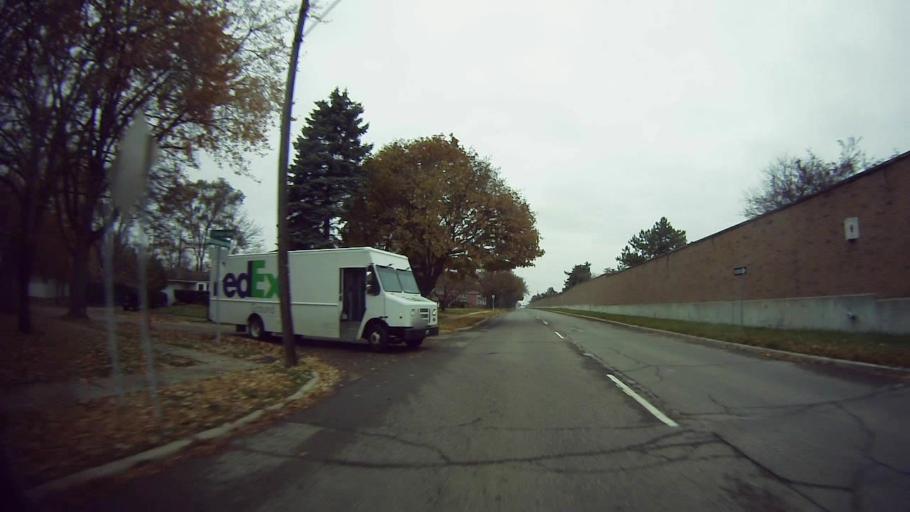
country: US
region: Michigan
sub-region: Oakland County
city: Madison Heights
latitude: 42.4944
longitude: -83.1175
